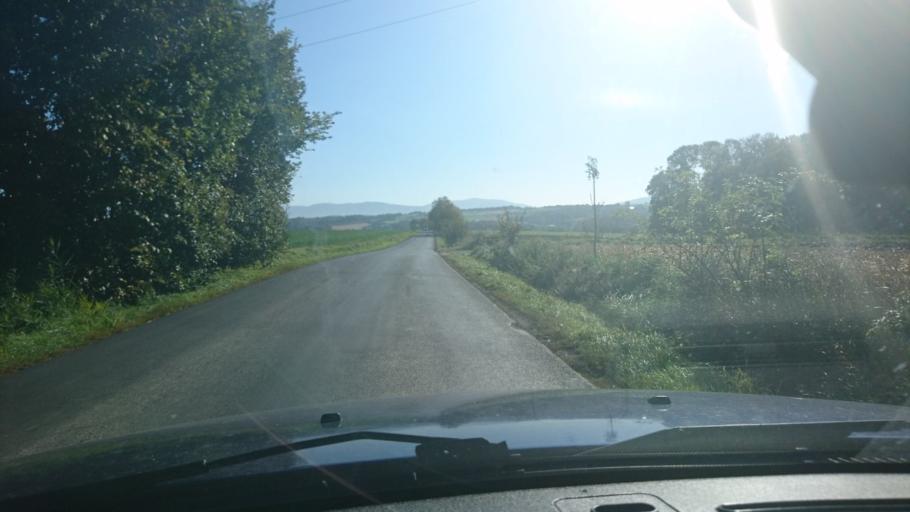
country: PL
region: Silesian Voivodeship
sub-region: Powiat bielski
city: Bronow
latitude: 49.8558
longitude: 18.9248
